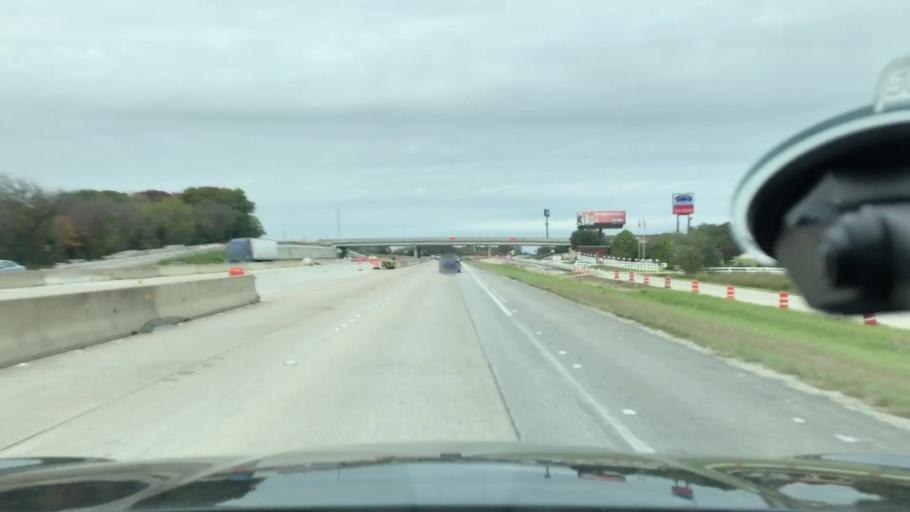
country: US
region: Texas
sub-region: Ellis County
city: Waxahachie
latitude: 32.3971
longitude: -96.8715
